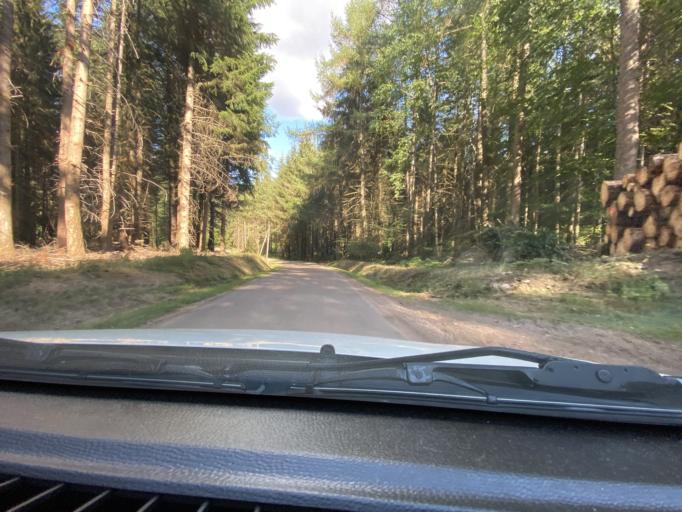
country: FR
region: Bourgogne
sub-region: Departement de la Cote-d'Or
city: Saulieu
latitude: 47.3081
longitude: 4.1895
